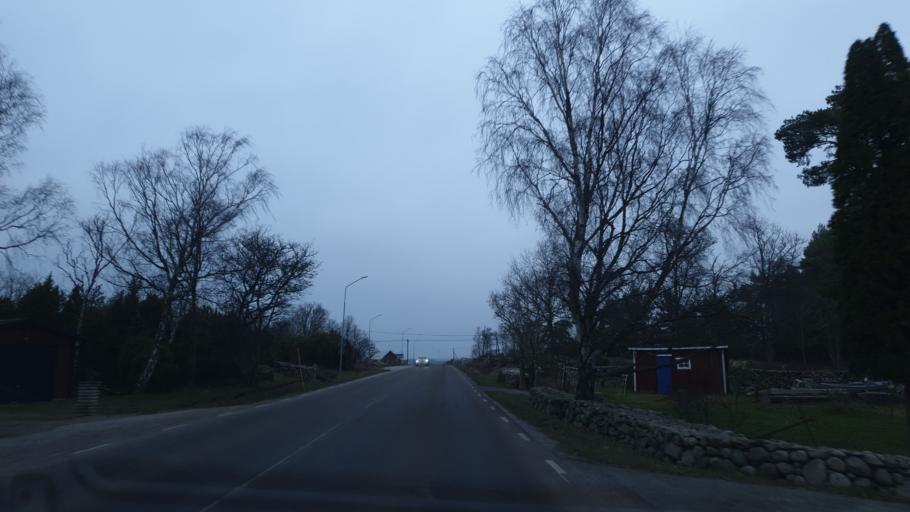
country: SE
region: Blekinge
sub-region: Karlskrona Kommun
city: Sturko
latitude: 56.1299
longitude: 15.7386
